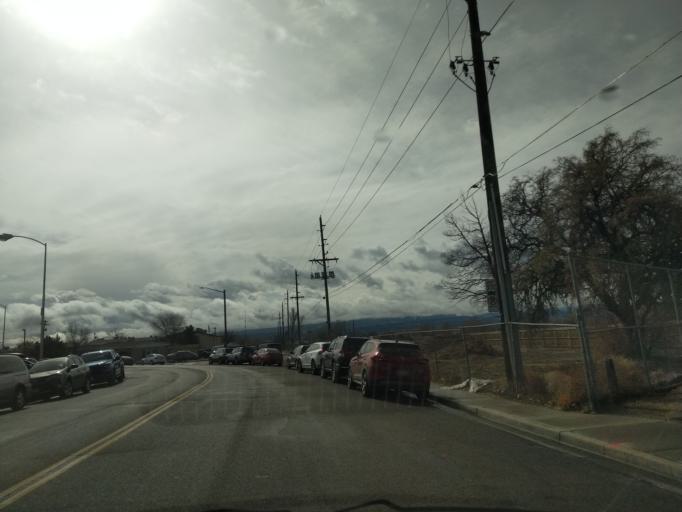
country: US
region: Colorado
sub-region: Mesa County
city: Grand Junction
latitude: 39.0764
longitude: -108.5385
